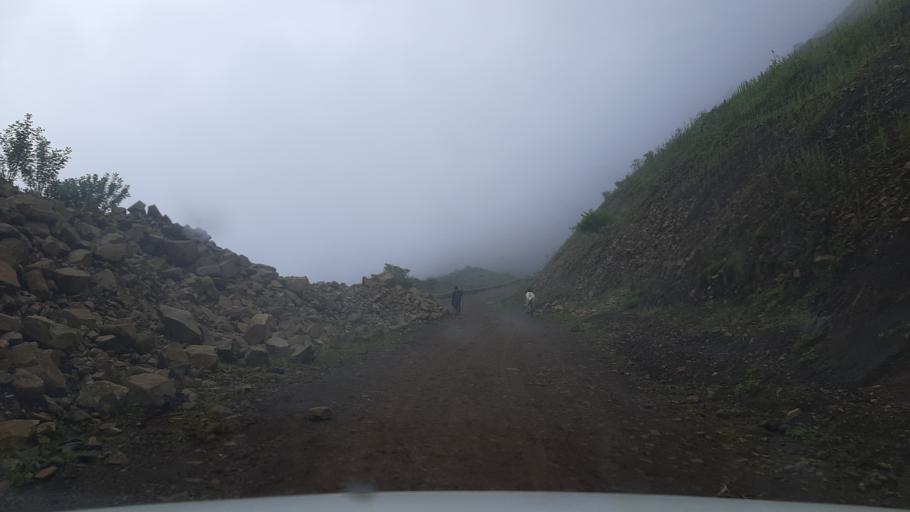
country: ET
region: Southern Nations, Nationalities, and People's Region
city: Bonga
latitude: 7.1128
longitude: 36.5664
